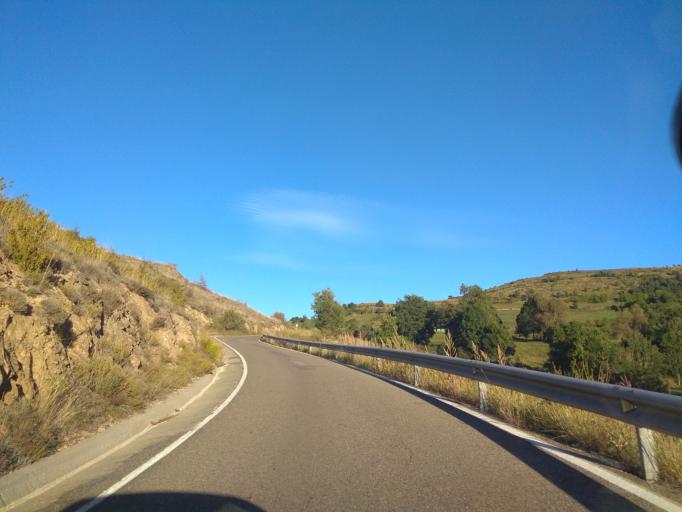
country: ES
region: Catalonia
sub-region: Provincia de Lleida
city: Lles de Cerdanya
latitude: 42.3505
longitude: 1.6904
